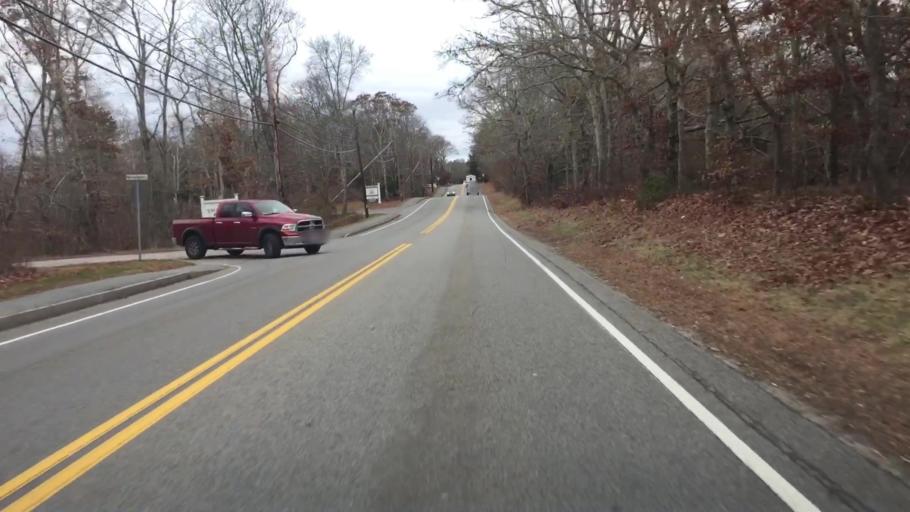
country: US
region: Massachusetts
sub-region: Barnstable County
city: Teaticket
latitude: 41.5728
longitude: -70.6057
